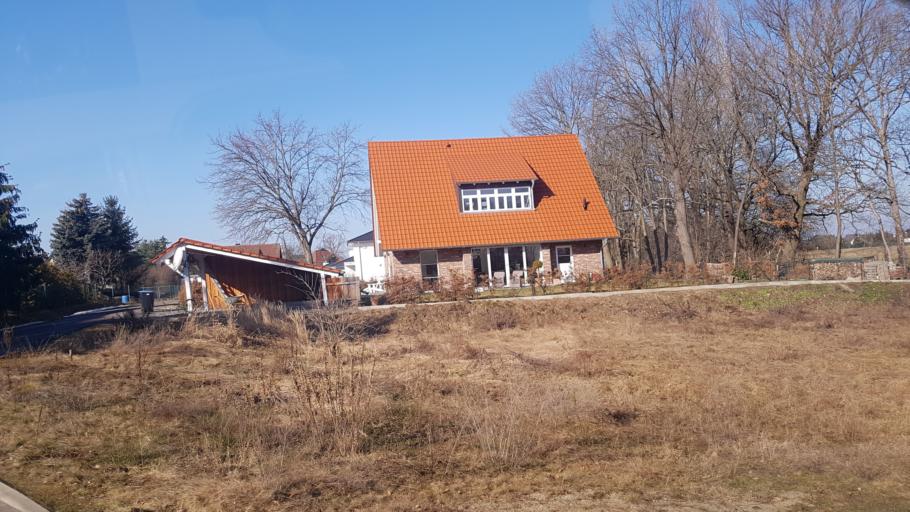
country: DE
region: Brandenburg
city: Senftenberg
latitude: 51.4947
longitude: 14.0669
